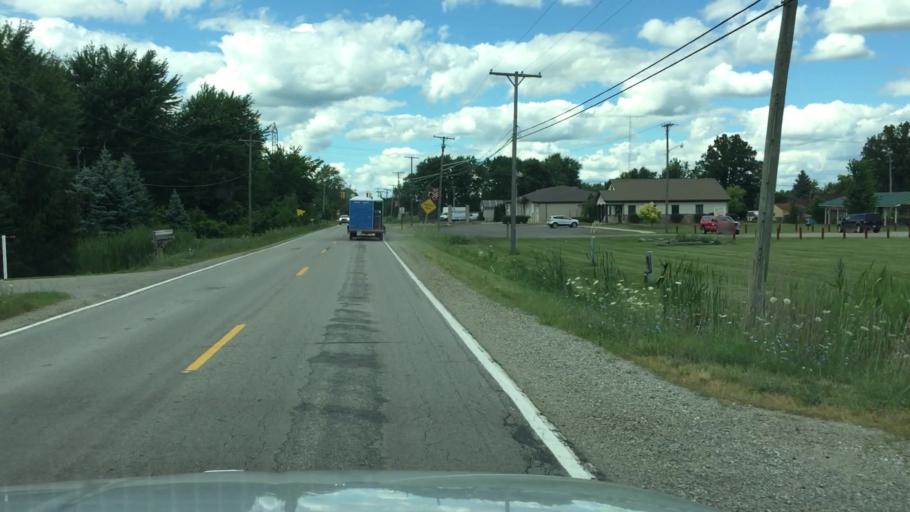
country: US
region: Michigan
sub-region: Macomb County
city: Armada
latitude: 42.9138
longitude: -82.9454
